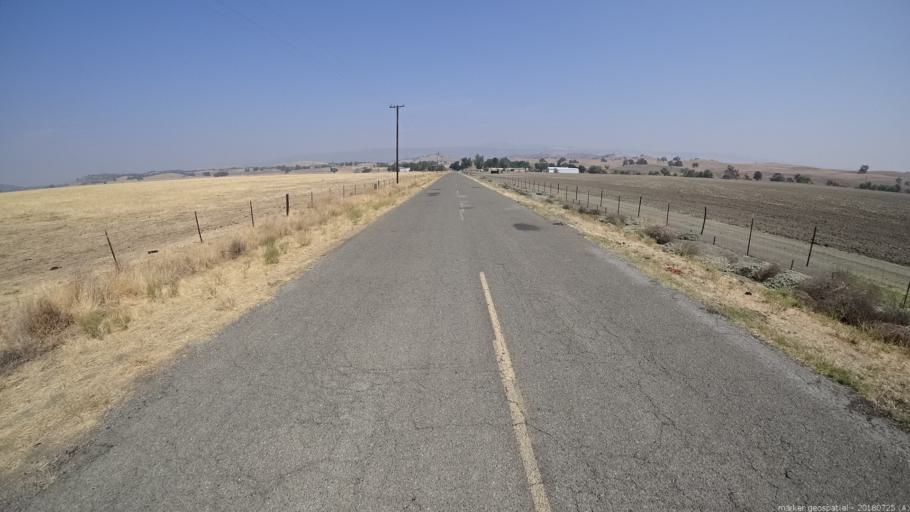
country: US
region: California
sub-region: San Luis Obispo County
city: Shandon
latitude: 35.8407
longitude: -120.3810
